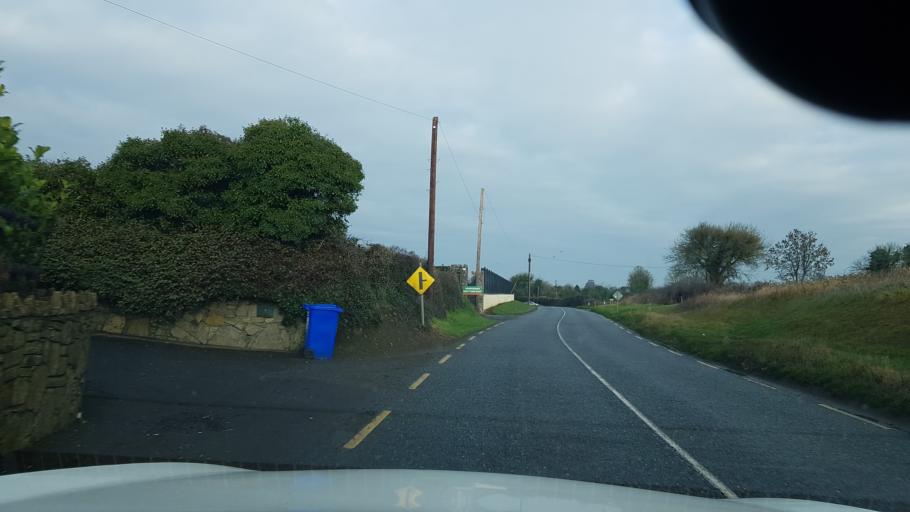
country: IE
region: Leinster
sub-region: An Mhi
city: Navan
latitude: 53.6814
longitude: -6.6741
